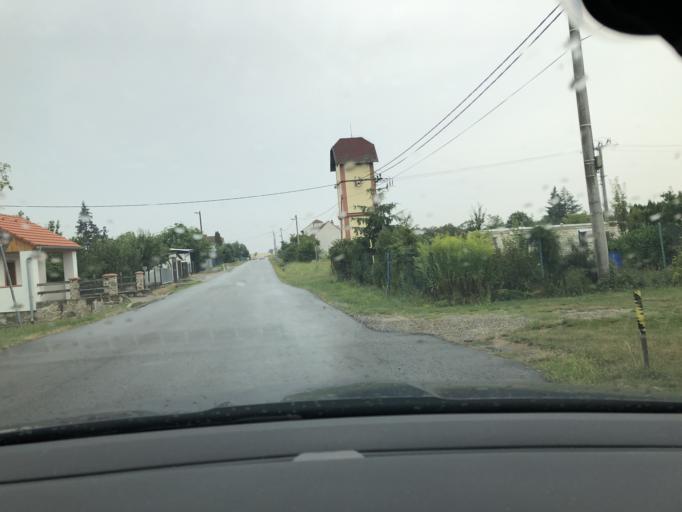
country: CZ
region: South Moravian
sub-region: Okres Znojmo
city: Jevisovice
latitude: 49.0288
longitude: 15.9770
